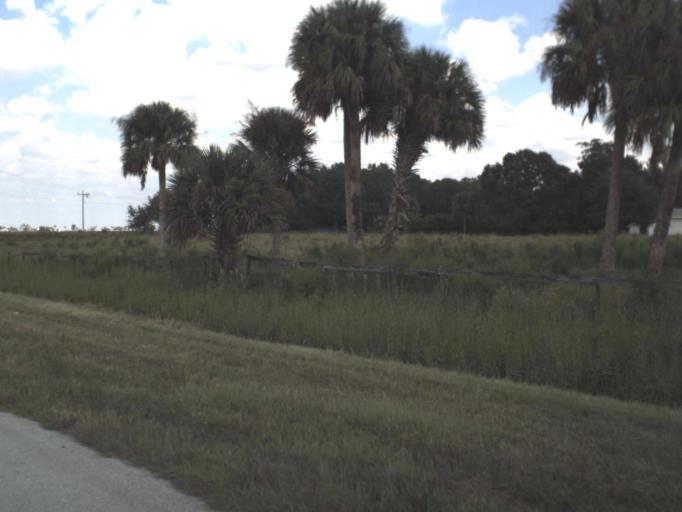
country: US
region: Florida
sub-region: Okeechobee County
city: Okeechobee
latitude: 27.3158
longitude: -80.9103
